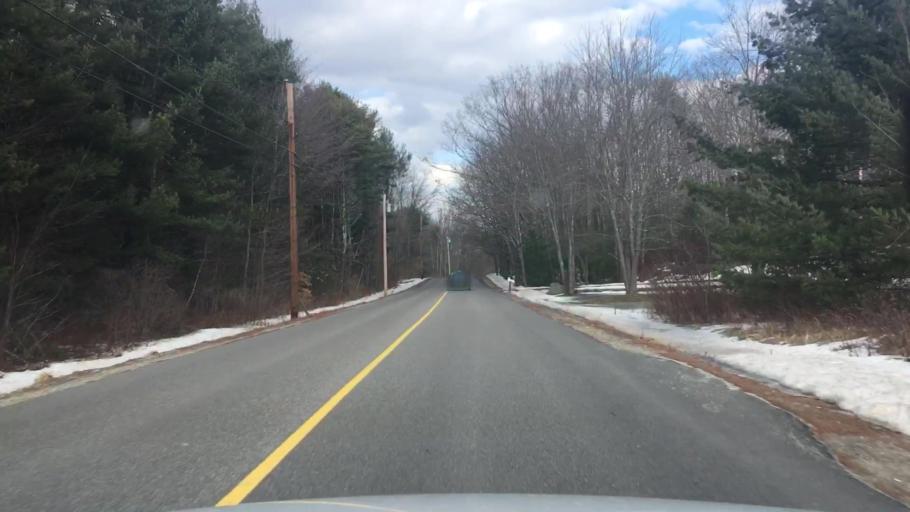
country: US
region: Maine
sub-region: York County
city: Arundel
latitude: 43.4148
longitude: -70.4717
